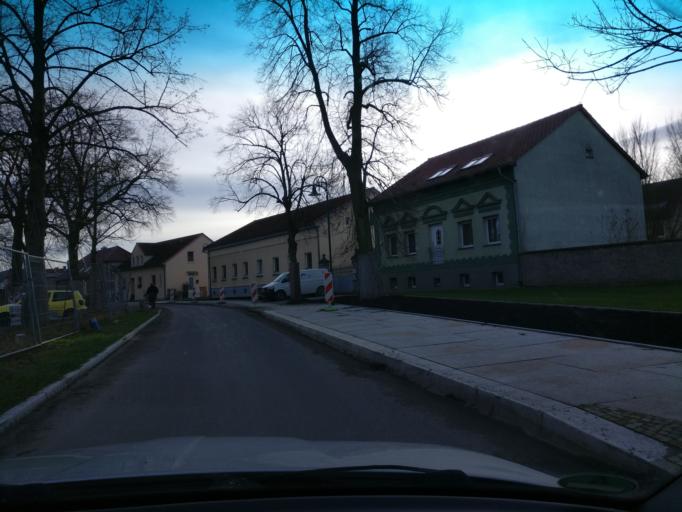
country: DE
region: Brandenburg
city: Bernau bei Berlin
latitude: 52.6793
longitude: 13.5333
